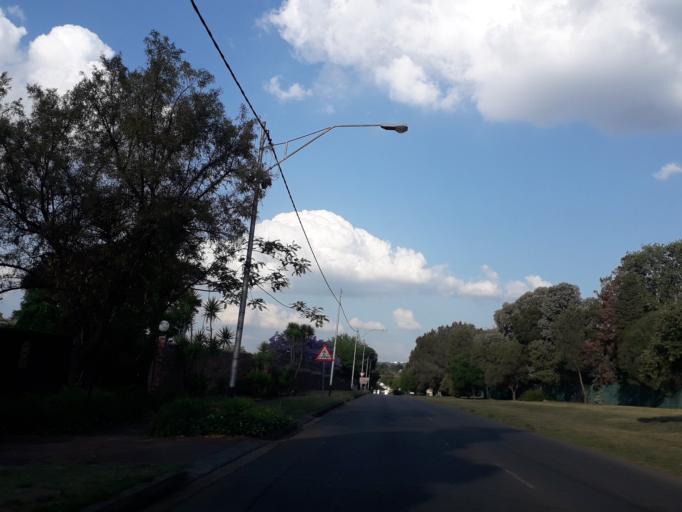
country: ZA
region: Gauteng
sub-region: City of Johannesburg Metropolitan Municipality
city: Johannesburg
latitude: -26.1517
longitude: 27.9992
